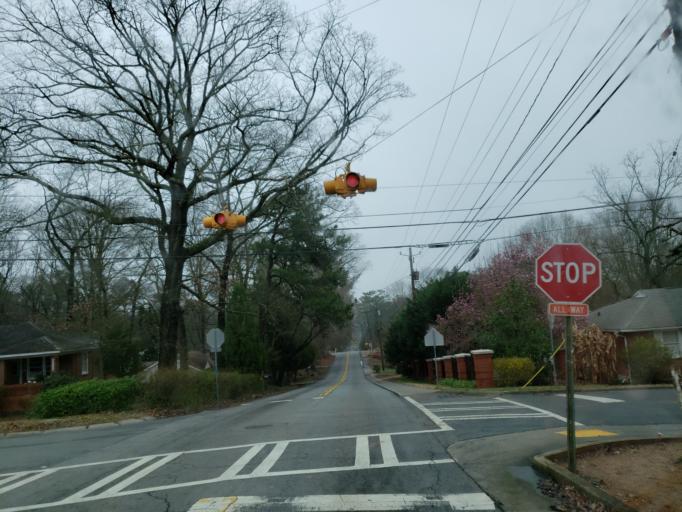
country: US
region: Georgia
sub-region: Cobb County
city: Fair Oaks
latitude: 33.9020
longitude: -84.5365
